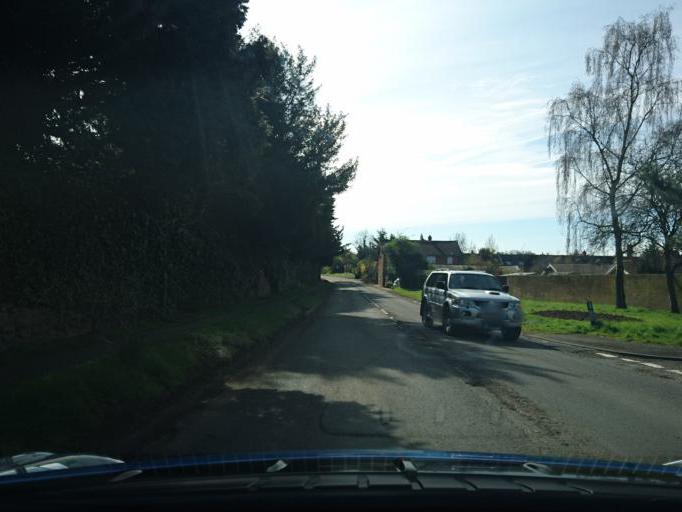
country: GB
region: England
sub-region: Herefordshire
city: Ledbury
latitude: 52.0313
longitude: -2.4194
